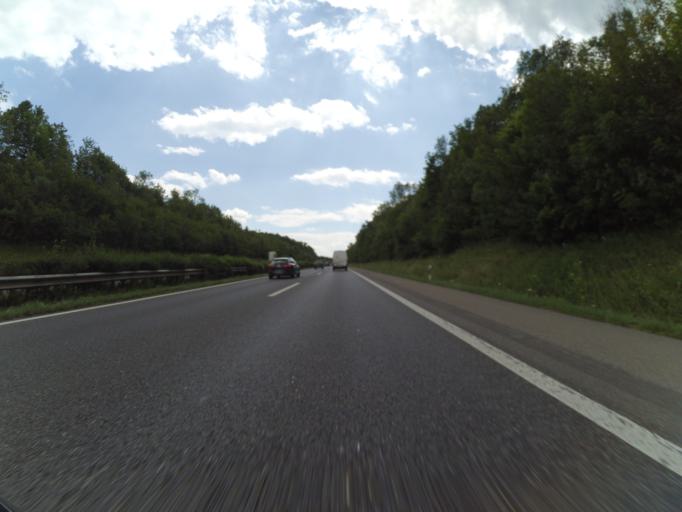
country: CH
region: Vaud
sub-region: Jura-Nord vaudois District
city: Bavois
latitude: 46.6662
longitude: 6.5708
